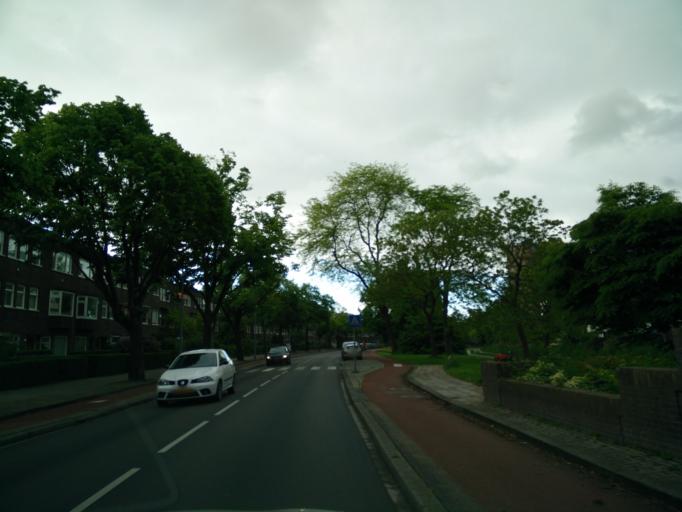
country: NL
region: Groningen
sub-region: Gemeente Groningen
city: Oosterpark
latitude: 53.2236
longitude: 6.5775
